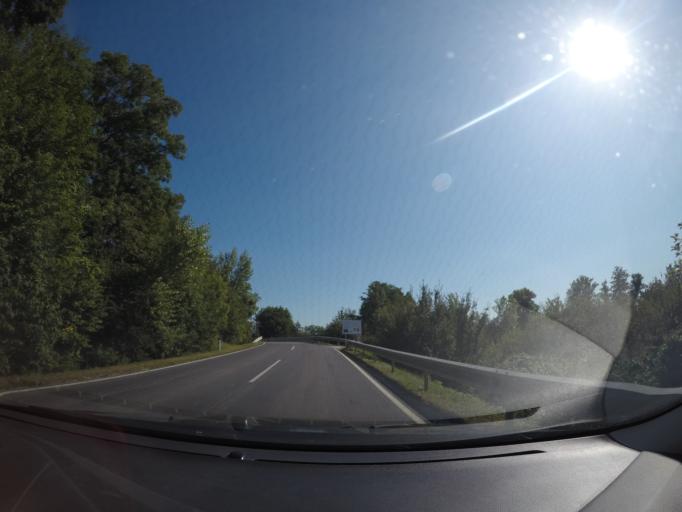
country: AT
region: Lower Austria
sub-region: Politischer Bezirk Baden
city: Seibersdorf
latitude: 47.9530
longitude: 16.5391
